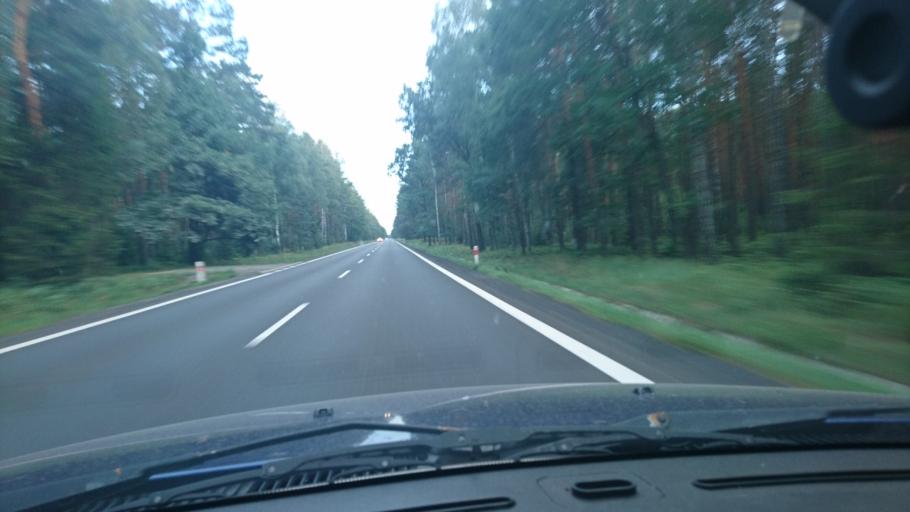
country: PL
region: Silesian Voivodeship
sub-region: Powiat tarnogorski
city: Tworog
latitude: 50.5695
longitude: 18.7111
